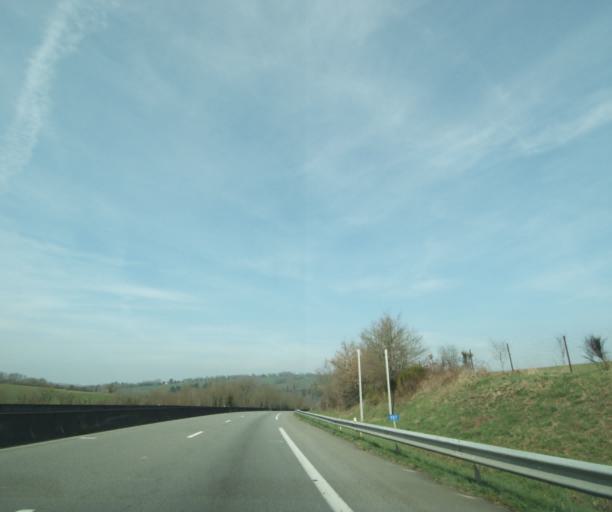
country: FR
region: Limousin
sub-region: Departement de la Haute-Vienne
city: Pierre-Buffiere
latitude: 45.7272
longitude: 1.3429
